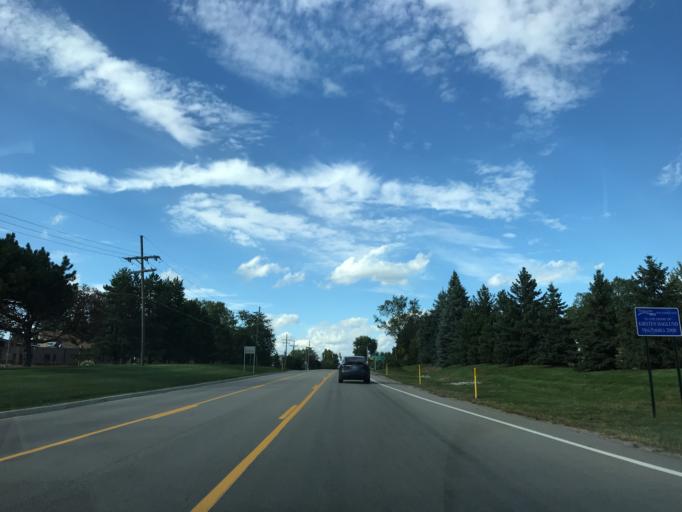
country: US
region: Michigan
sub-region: Oakland County
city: Farmington Hills
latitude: 42.5250
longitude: -83.3992
